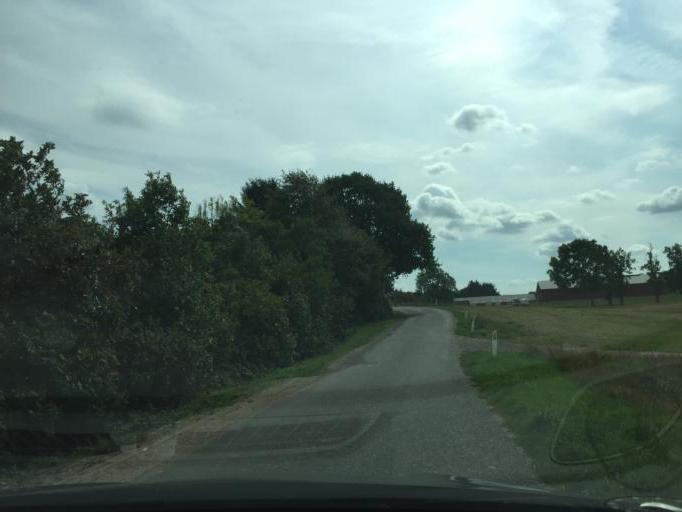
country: DK
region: South Denmark
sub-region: Assens Kommune
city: Tommerup Stationsby
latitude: 55.4046
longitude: 10.2338
